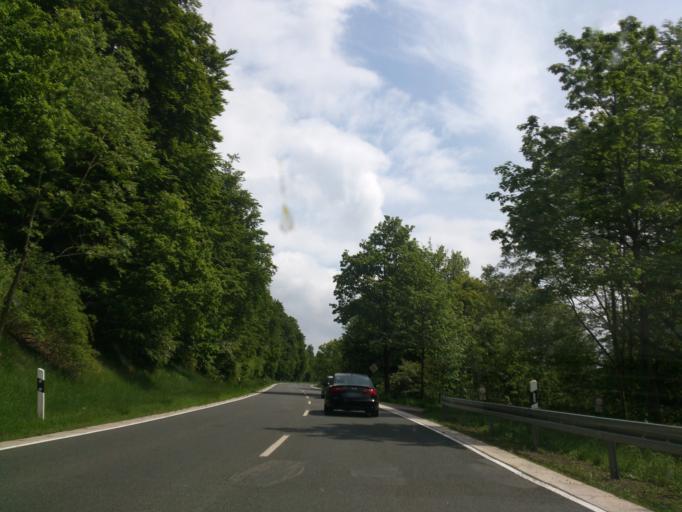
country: DE
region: Hesse
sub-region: Regierungsbezirk Kassel
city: Martinhagen
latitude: 51.3142
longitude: 9.3383
